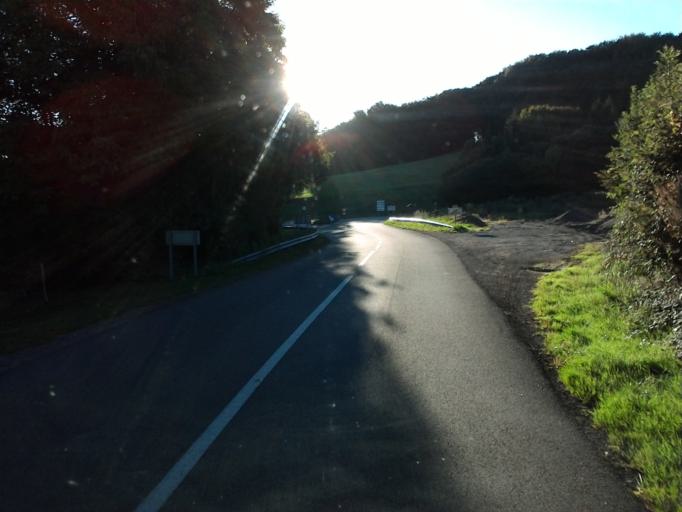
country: FR
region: Bourgogne
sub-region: Departement de la Nievre
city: Lormes
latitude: 47.2843
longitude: 4.0184
